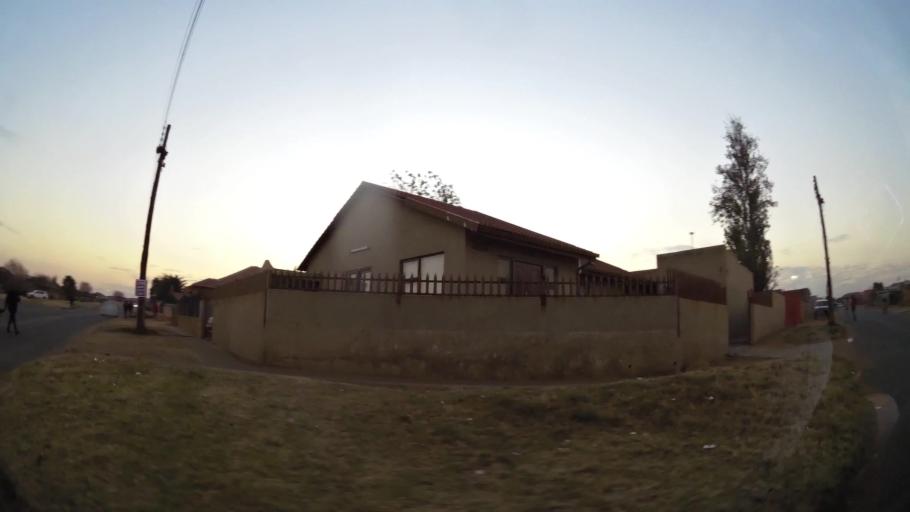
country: ZA
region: Gauteng
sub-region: West Rand District Municipality
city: Randfontein
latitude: -26.2090
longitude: 27.7117
